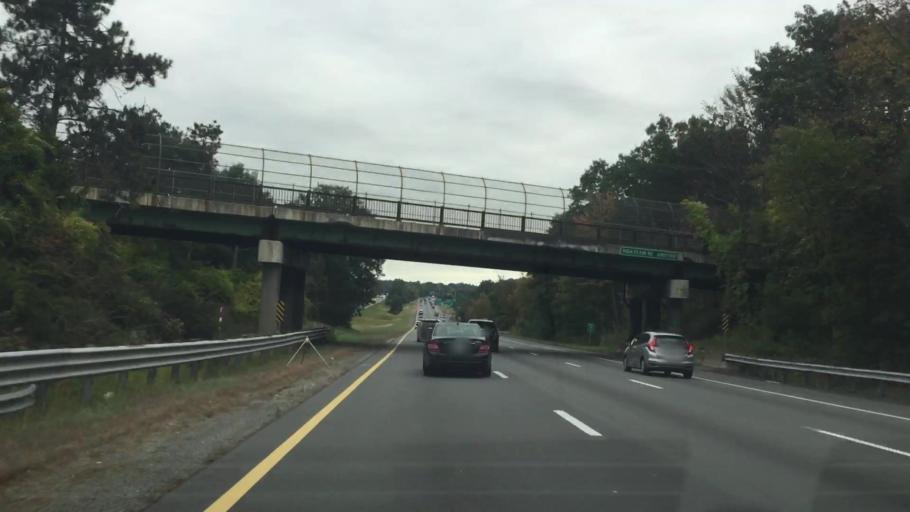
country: US
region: Massachusetts
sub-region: Middlesex County
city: Tewksbury
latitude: 42.6584
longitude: -71.2015
